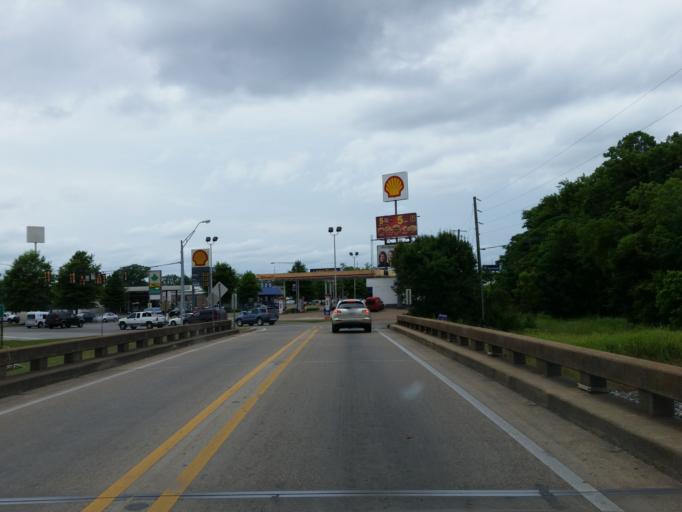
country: US
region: Mississippi
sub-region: Lauderdale County
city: Meridian
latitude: 32.3557
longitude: -88.6920
